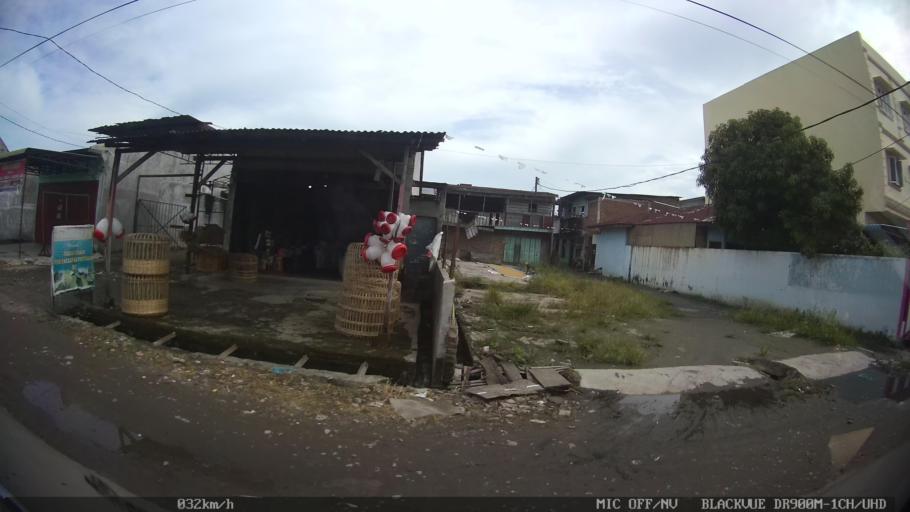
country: ID
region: North Sumatra
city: Medan
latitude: 3.6203
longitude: 98.7381
